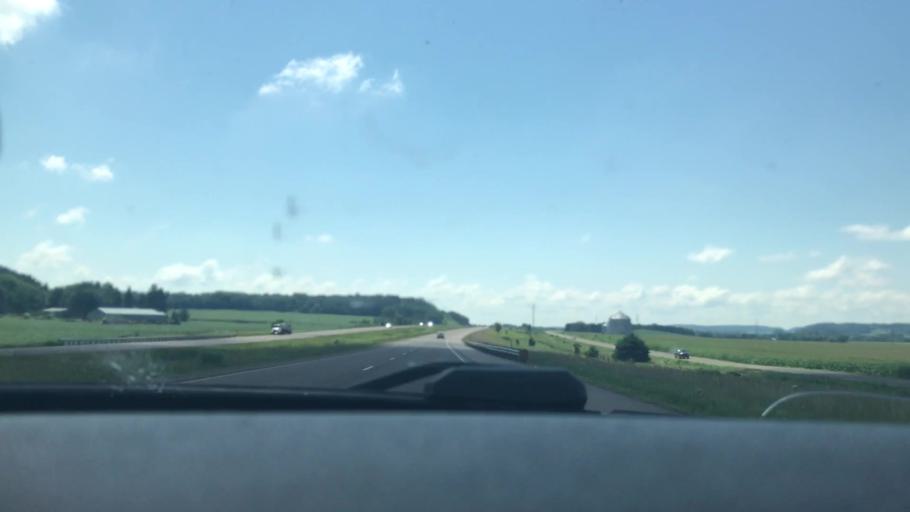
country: US
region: Wisconsin
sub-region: Chippewa County
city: Bloomer
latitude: 45.0368
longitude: -91.4552
